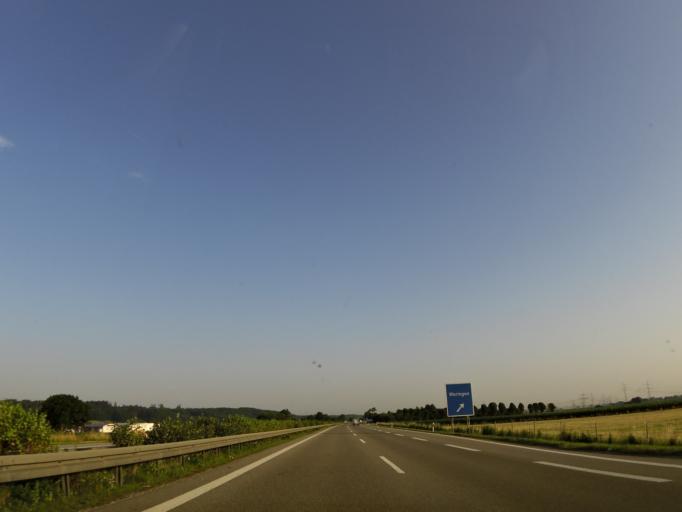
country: DE
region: Bavaria
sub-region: Swabia
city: Woringen
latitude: 47.9225
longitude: 10.2182
